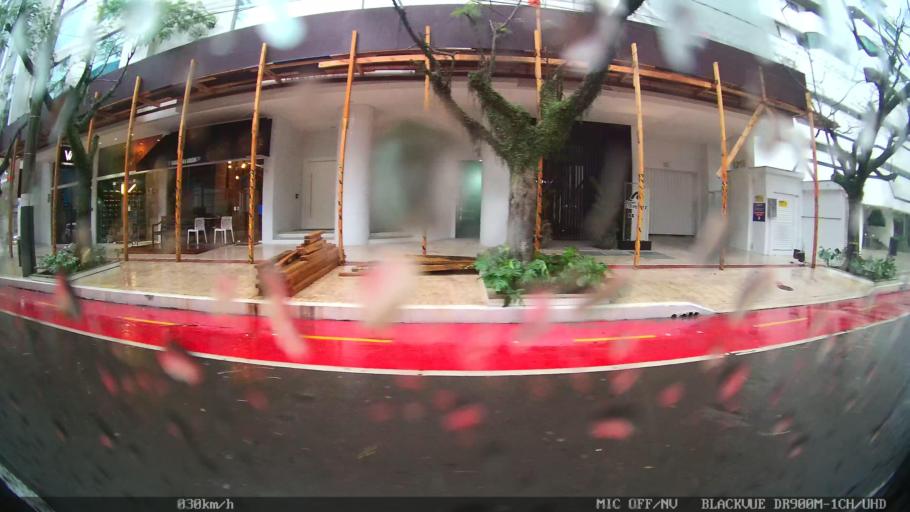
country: BR
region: Santa Catarina
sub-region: Balneario Camboriu
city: Balneario Camboriu
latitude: -27.0075
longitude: -48.6081
